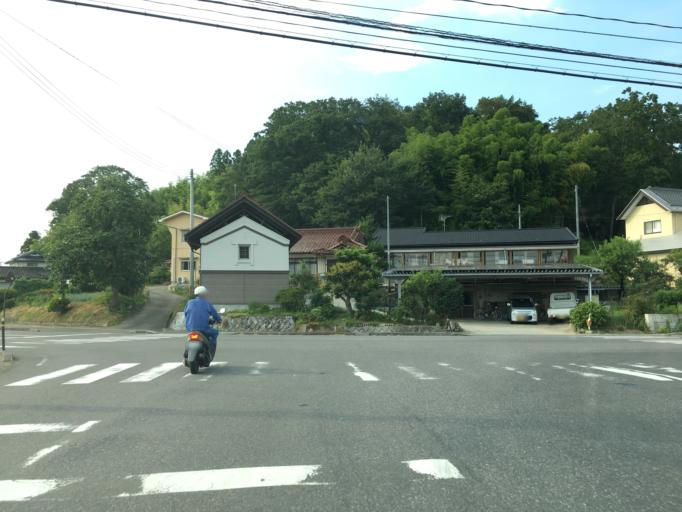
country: JP
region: Fukushima
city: Motomiya
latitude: 37.5072
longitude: 140.4343
